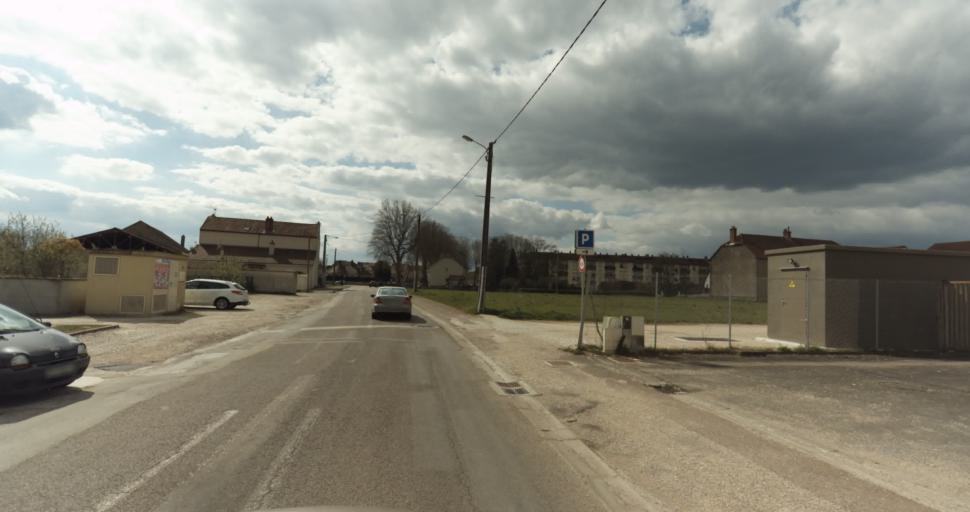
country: FR
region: Bourgogne
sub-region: Departement de la Cote-d'Or
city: Auxonne
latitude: 47.1938
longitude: 5.3952
